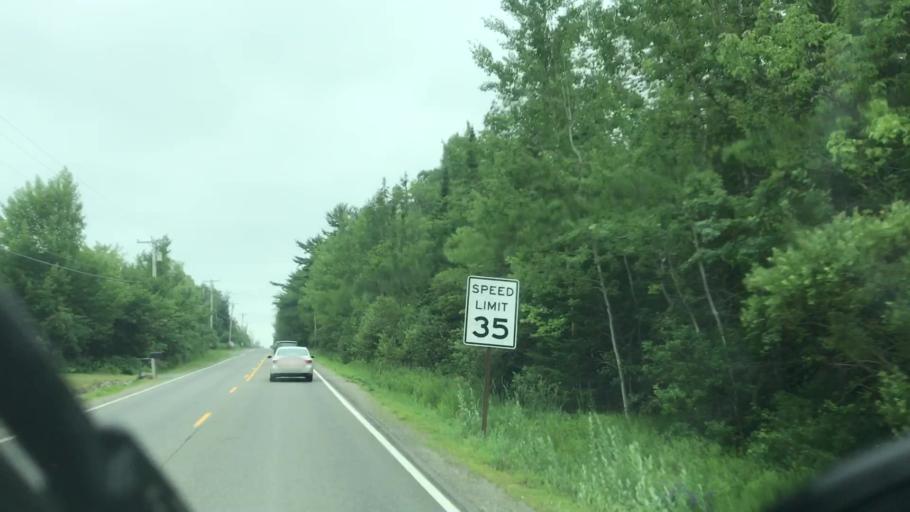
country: US
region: Maine
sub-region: Penobscot County
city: Veazie
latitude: 44.8496
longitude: -68.7370
